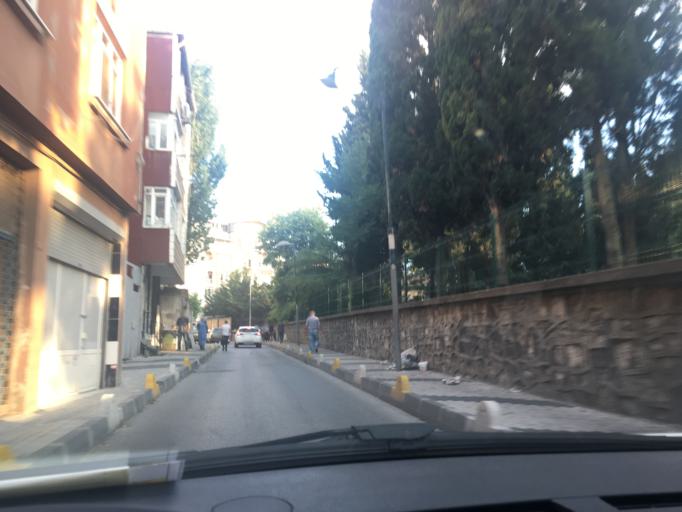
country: TR
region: Istanbul
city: Sisli
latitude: 41.0520
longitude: 28.9751
